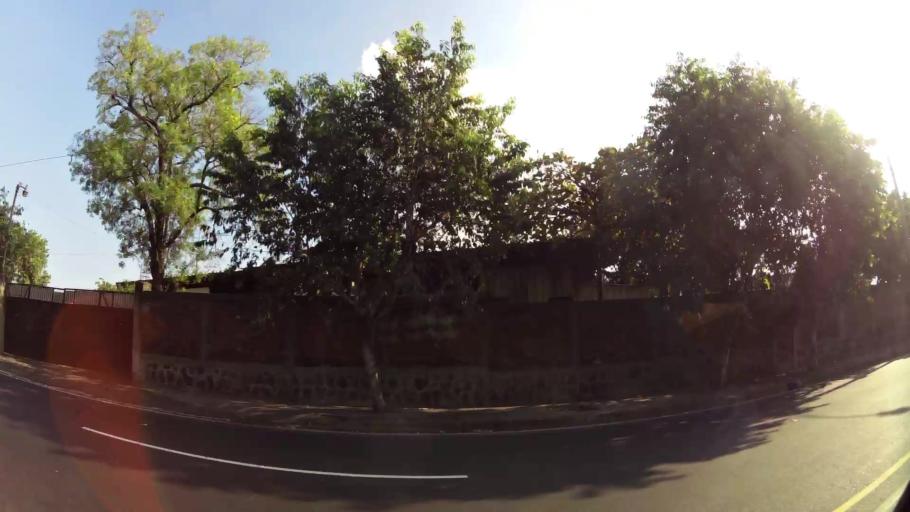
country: SV
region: San Salvador
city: San Salvador
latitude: 13.6963
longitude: -89.1755
